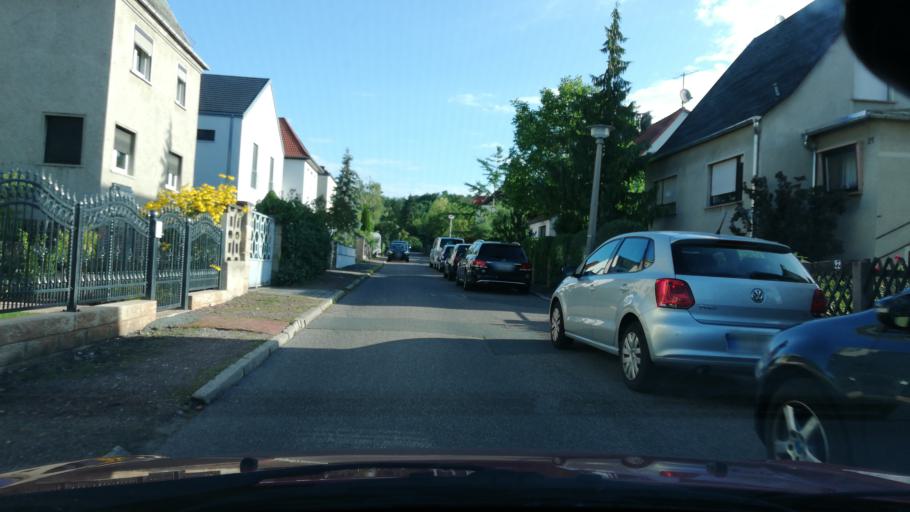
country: DE
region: Saxony-Anhalt
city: Halle Neustadt
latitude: 51.4933
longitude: 11.9095
